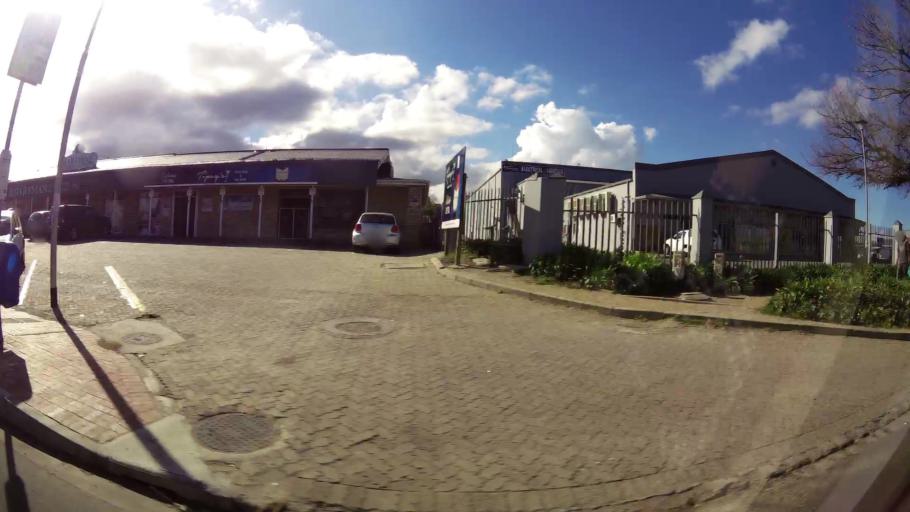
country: ZA
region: Western Cape
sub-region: Eden District Municipality
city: George
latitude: -33.9633
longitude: 22.4771
